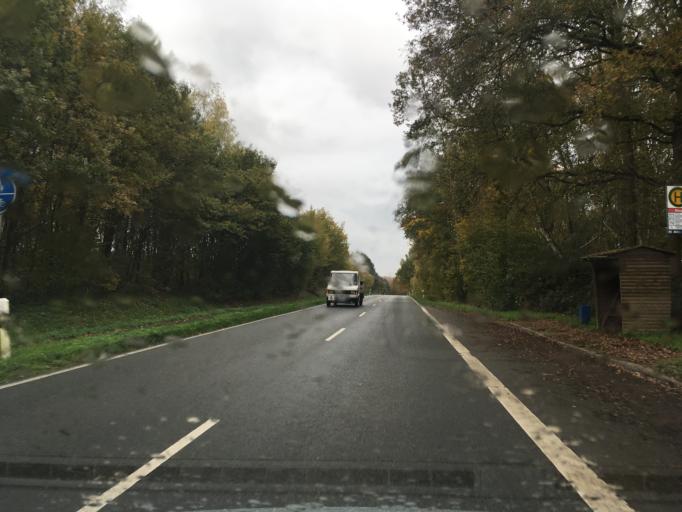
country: DE
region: North Rhine-Westphalia
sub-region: Regierungsbezirk Munster
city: Klein Reken
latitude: 51.8185
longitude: 7.0999
